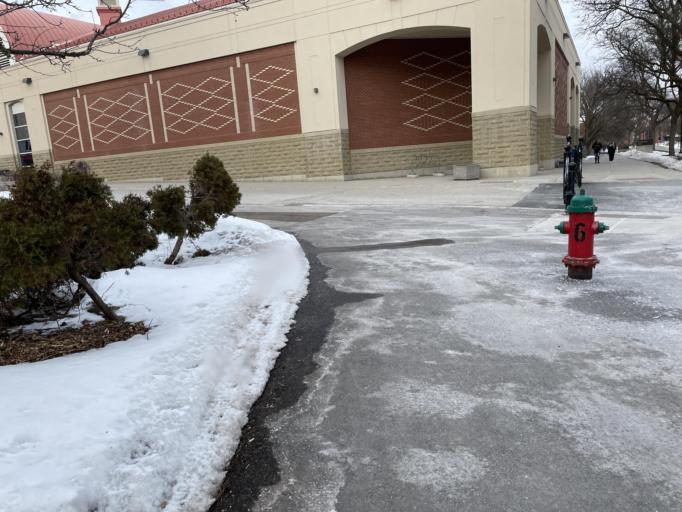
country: CA
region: Ontario
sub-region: Wellington County
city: Guelph
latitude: 43.5317
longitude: -80.2260
